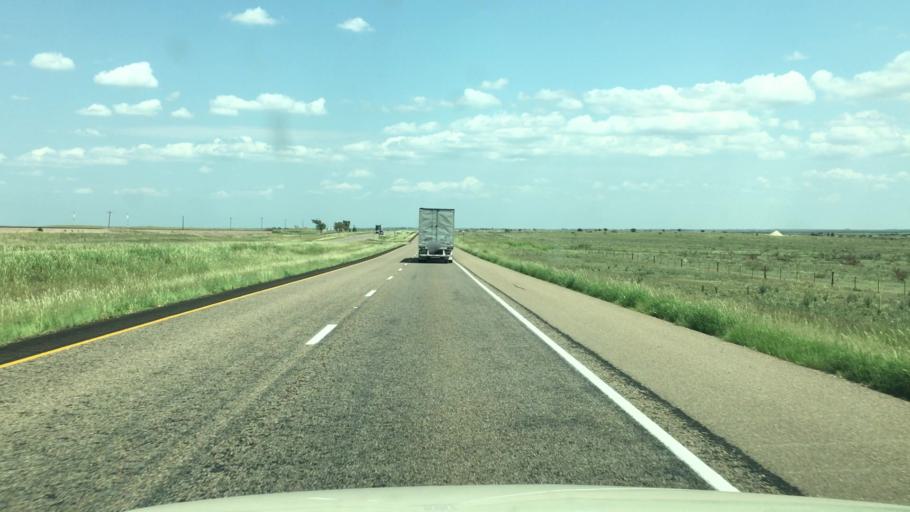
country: US
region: Texas
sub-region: Armstrong County
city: Claude
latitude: 35.0324
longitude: -101.1435
